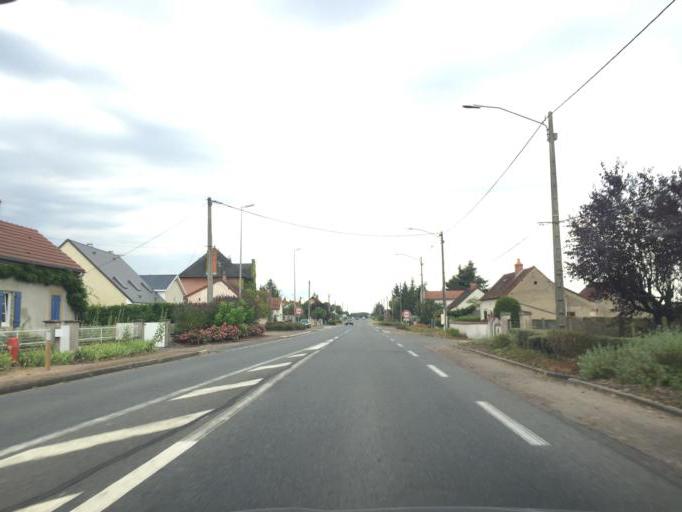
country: FR
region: Auvergne
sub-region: Departement de l'Allier
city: Bessay-sur-Allier
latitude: 46.4372
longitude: 3.3612
